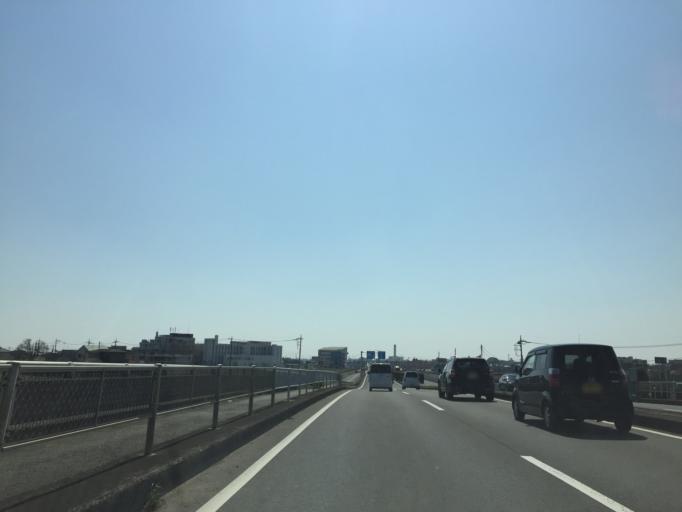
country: JP
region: Saitama
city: Kamifukuoka
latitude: 35.8801
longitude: 139.5357
